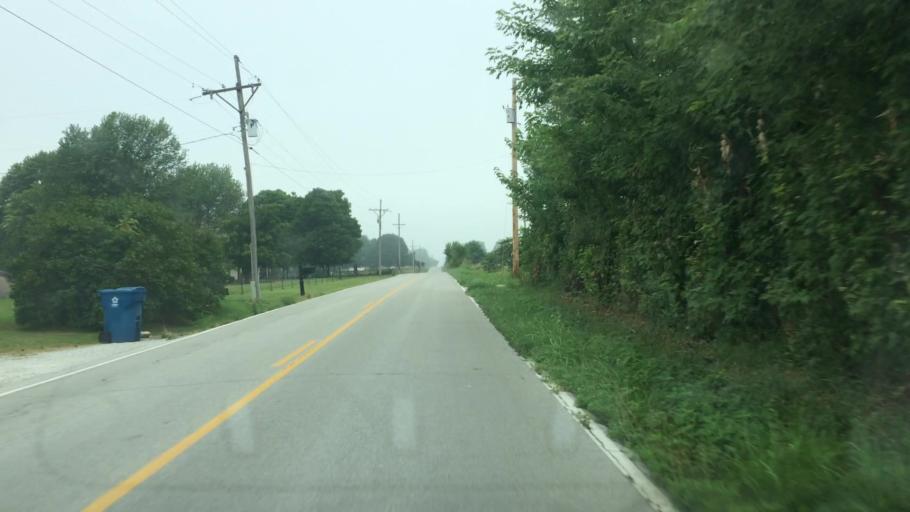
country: US
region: Missouri
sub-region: Greene County
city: Strafford
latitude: 37.2713
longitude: -93.1529
